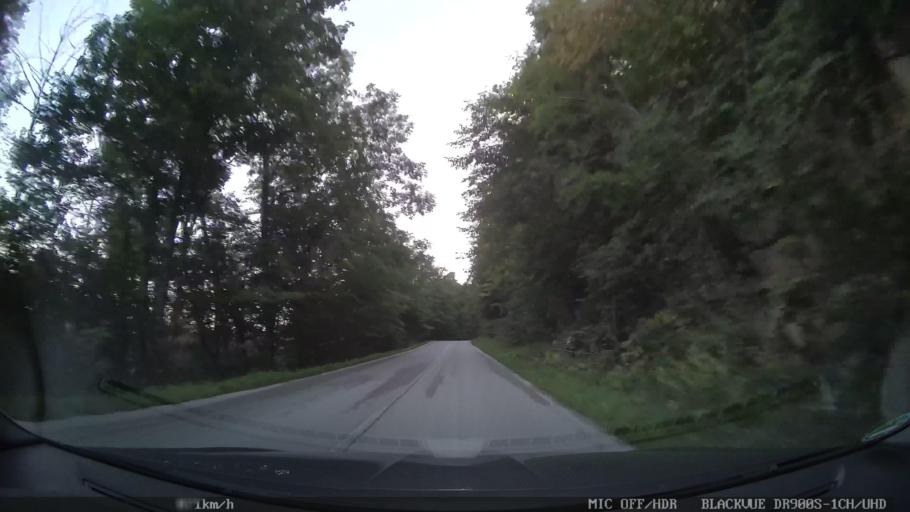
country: HR
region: Primorsko-Goranska
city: Vrbovsko
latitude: 45.1915
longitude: 15.0000
